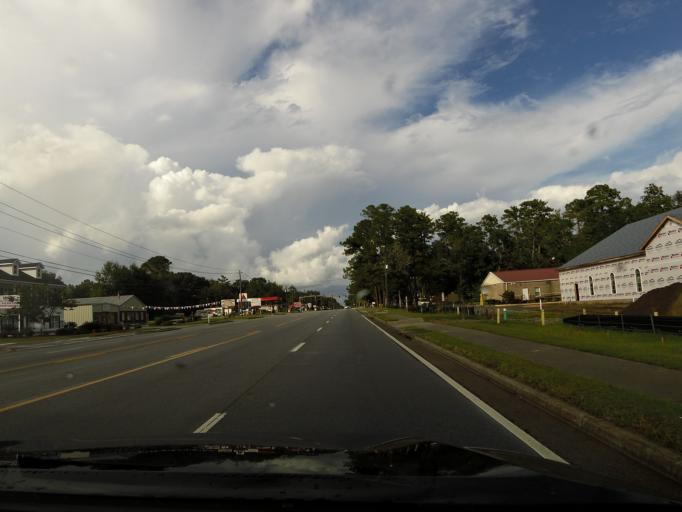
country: US
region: Georgia
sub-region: Liberty County
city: Walthourville
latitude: 31.7938
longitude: -81.6073
